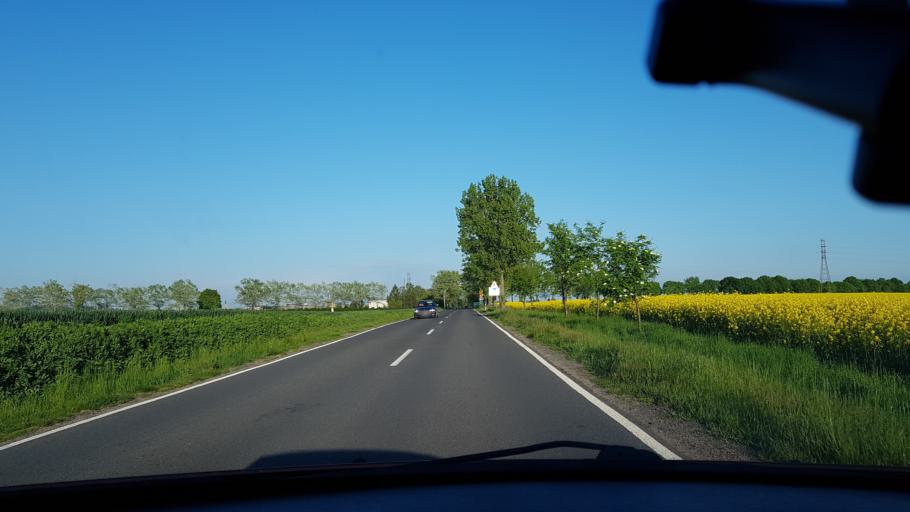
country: PL
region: Lower Silesian Voivodeship
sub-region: Powiat zabkowicki
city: Zabkowice Slaskie
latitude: 50.5949
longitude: 16.7817
